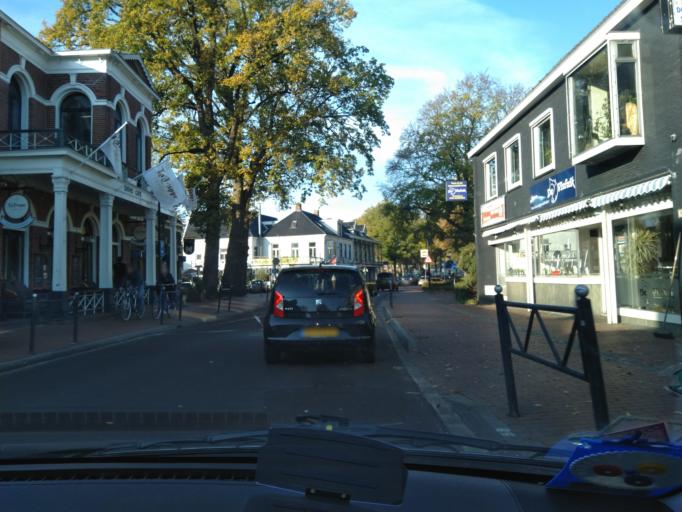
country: NL
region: Drenthe
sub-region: Gemeente Tynaarlo
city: Zuidlaren
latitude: 53.0947
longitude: 6.6872
